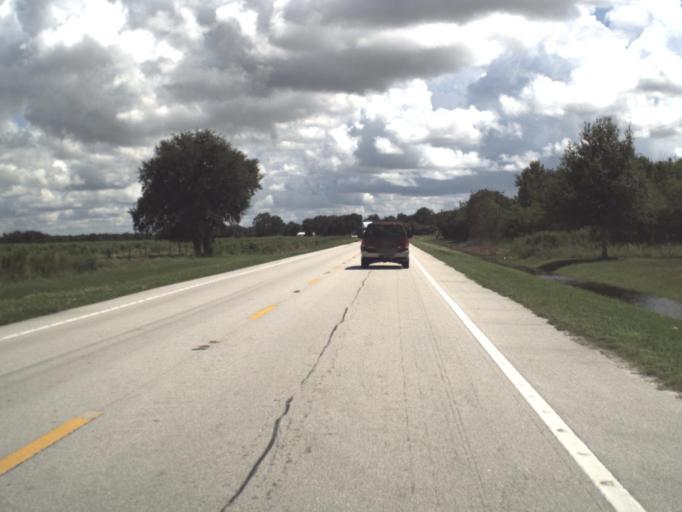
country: US
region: Florida
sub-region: DeSoto County
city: Arcadia
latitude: 27.2325
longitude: -81.9264
